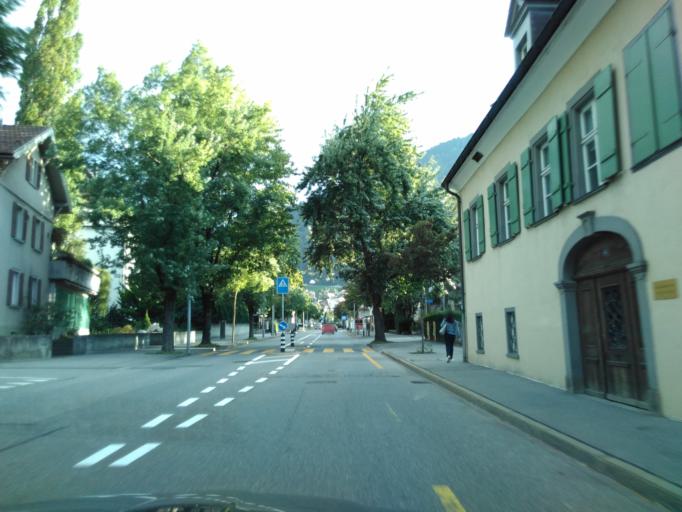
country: CH
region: Grisons
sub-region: Plessur District
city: Chur
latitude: 46.8549
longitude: 9.5348
